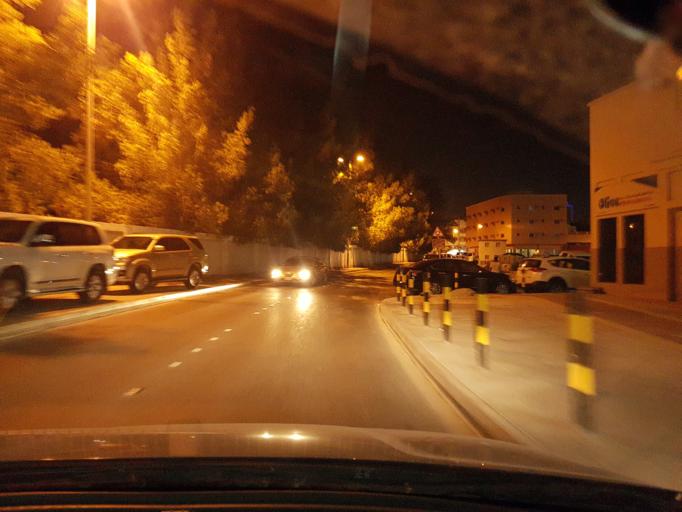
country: BH
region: Manama
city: Manama
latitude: 26.2297
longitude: 50.5853
